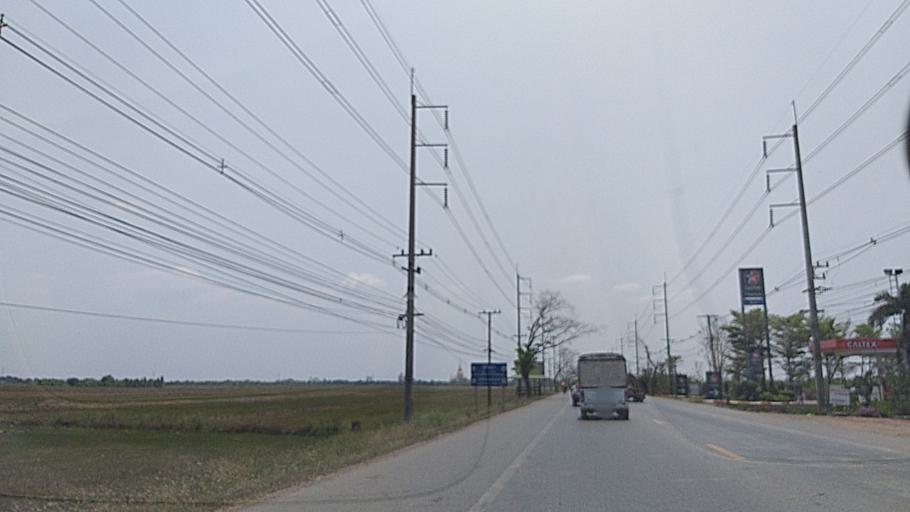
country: TH
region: Chachoengsao
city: Bang Nam Priao
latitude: 13.8183
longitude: 101.0536
